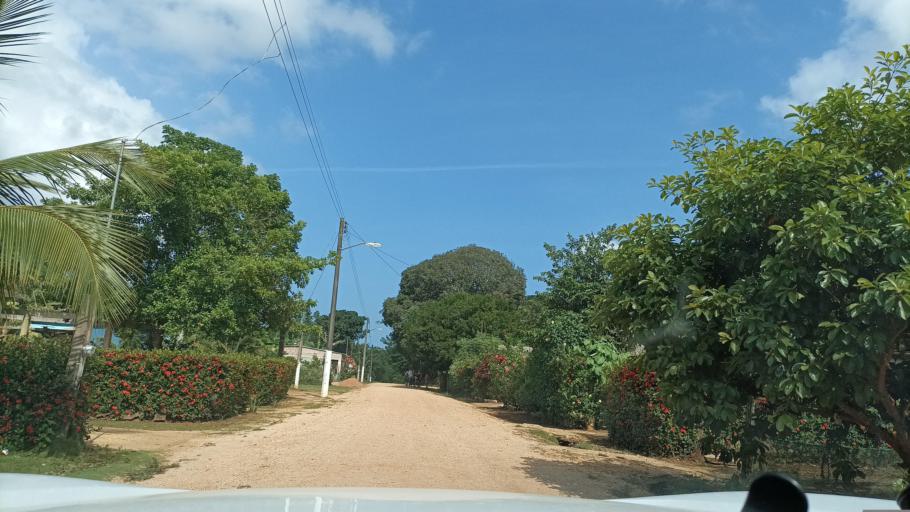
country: MX
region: Veracruz
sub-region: Chinameca
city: Chacalapa
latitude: 18.0819
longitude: -94.6728
